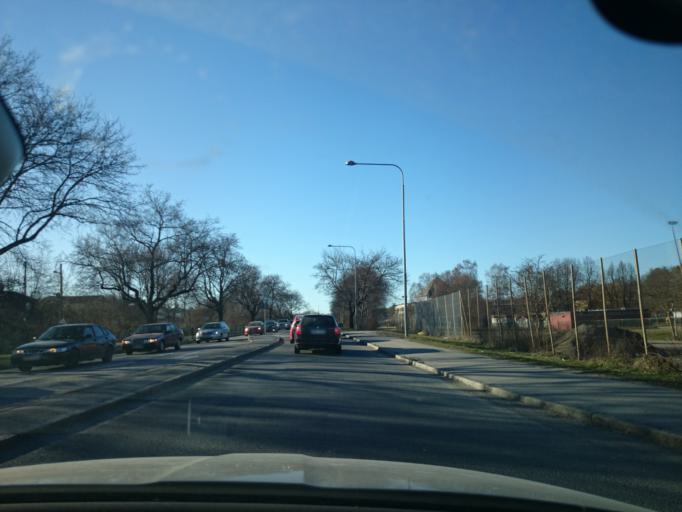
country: SE
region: Stockholm
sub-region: Huddinge Kommun
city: Huddinge
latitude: 59.2820
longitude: 17.9981
